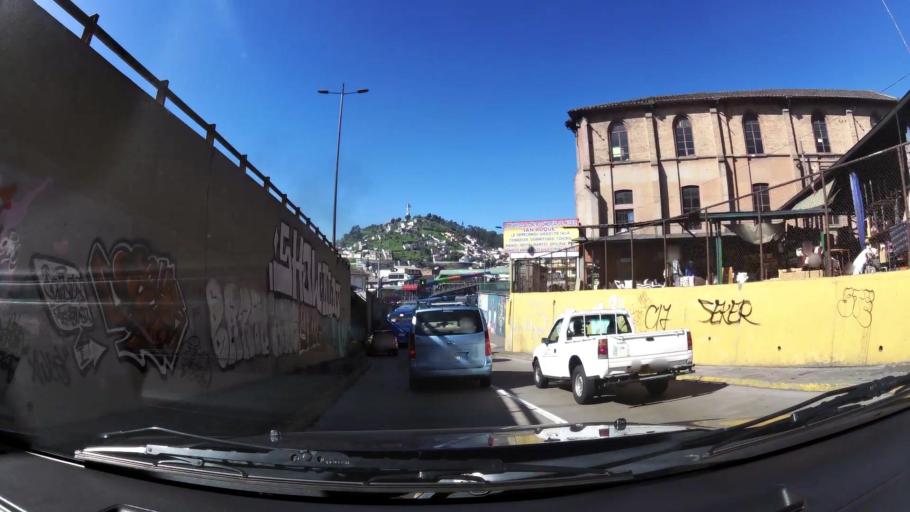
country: EC
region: Pichincha
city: Quito
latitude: -0.2199
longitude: -78.5207
